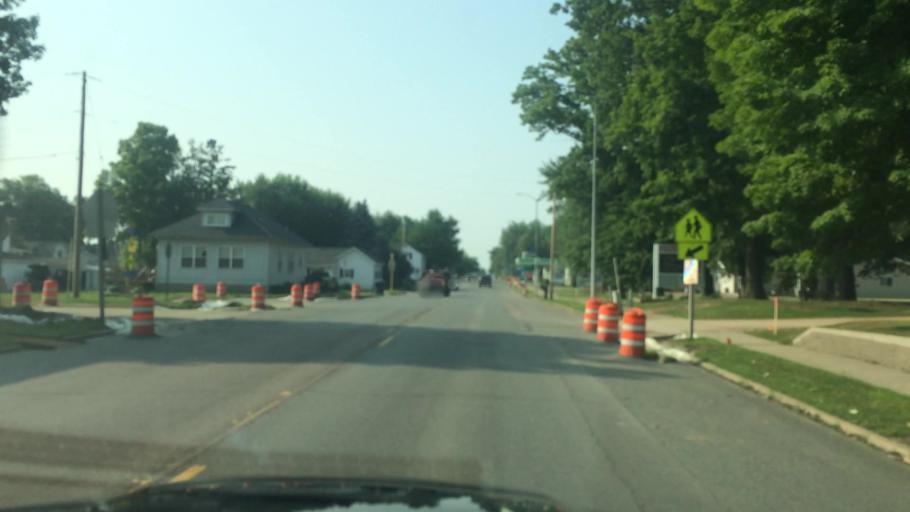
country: US
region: Wisconsin
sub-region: Marathon County
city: Stratford
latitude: 44.8055
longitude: -90.0792
